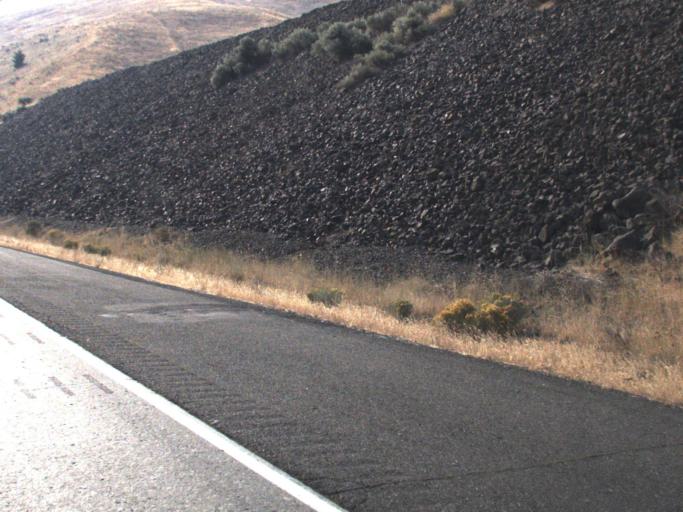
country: US
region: Washington
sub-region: Kittitas County
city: Kittitas
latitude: 46.8939
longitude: -120.4453
